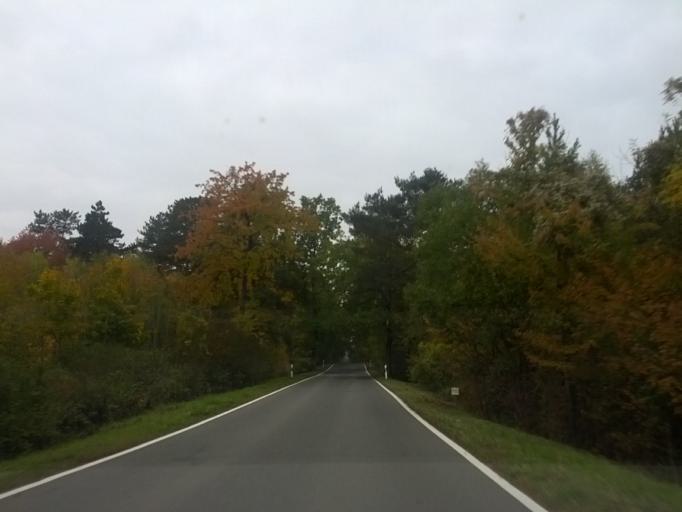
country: DE
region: Thuringia
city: Creuzburg
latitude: 51.0258
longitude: 10.2138
